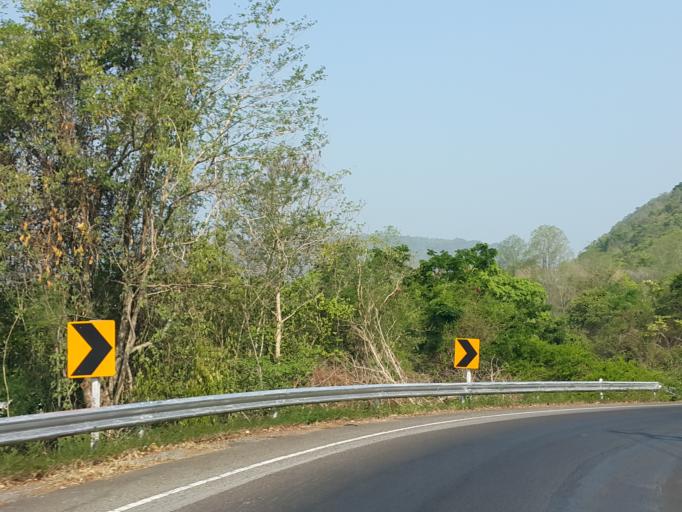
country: TH
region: Kanchanaburi
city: Sai Yok
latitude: 14.1186
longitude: 99.1473
